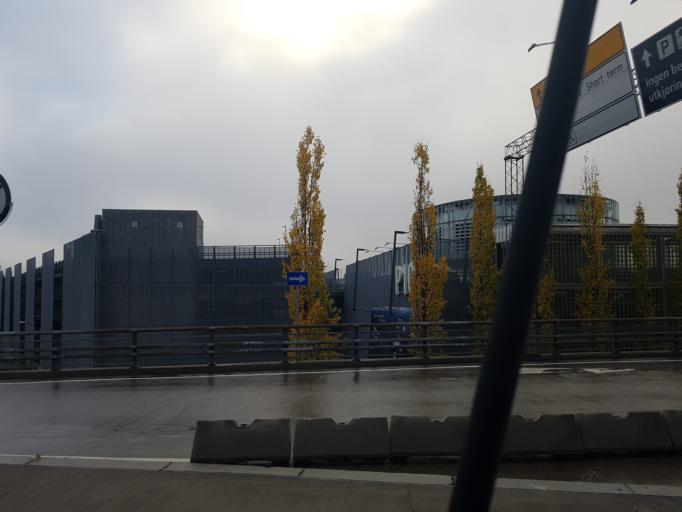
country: NO
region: Akershus
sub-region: Nannestad
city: Teigebyen
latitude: 60.1930
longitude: 11.1014
